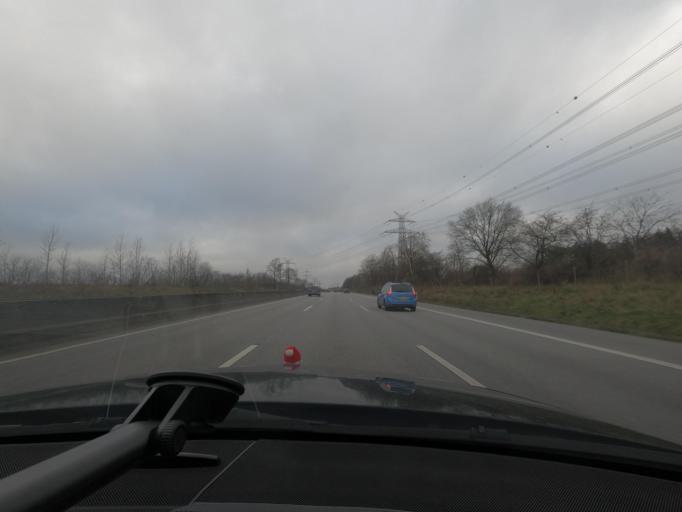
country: DE
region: Schleswig-Holstein
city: Alveslohe
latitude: 53.7762
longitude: 9.9435
